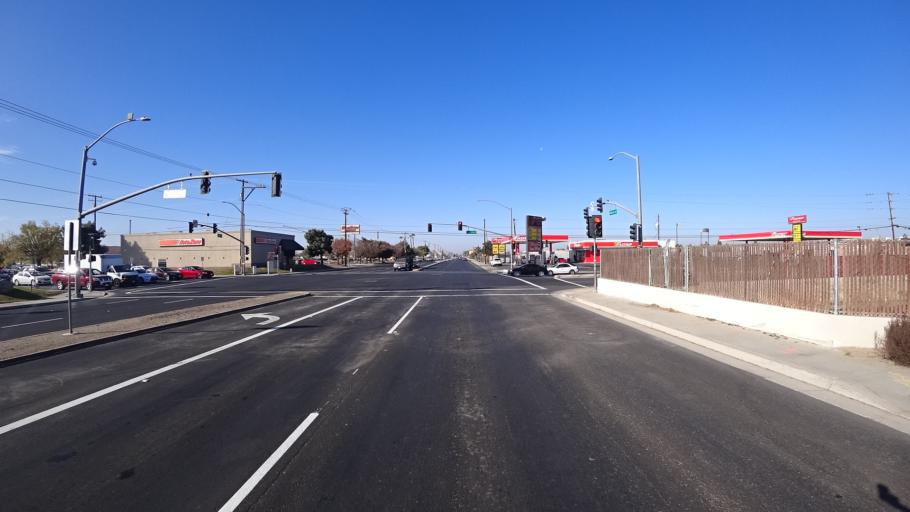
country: US
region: California
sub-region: Kern County
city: Greenfield
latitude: 35.3177
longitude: -119.0209
